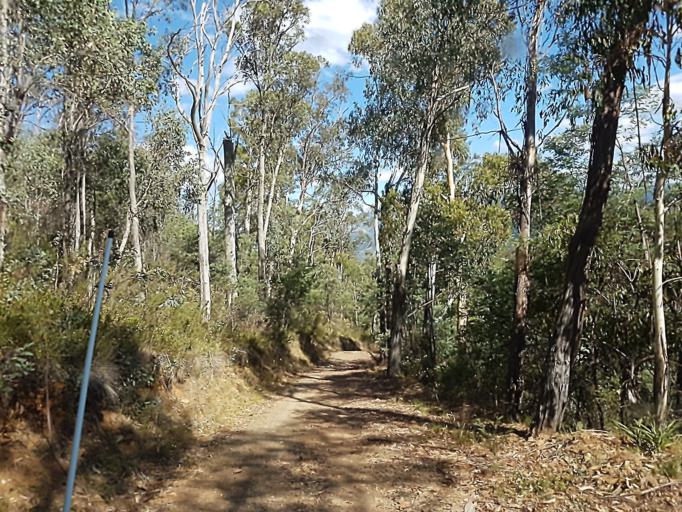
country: AU
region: Victoria
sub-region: Alpine
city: Mount Beauty
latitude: -36.8912
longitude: 147.0264
